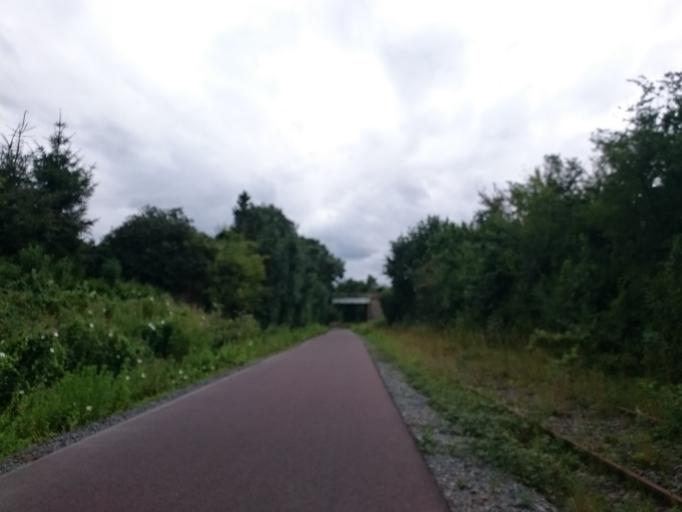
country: FR
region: Lower Normandy
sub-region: Departement du Calvados
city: Saint-Andre-sur-Orne
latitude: 49.1330
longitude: -0.4002
